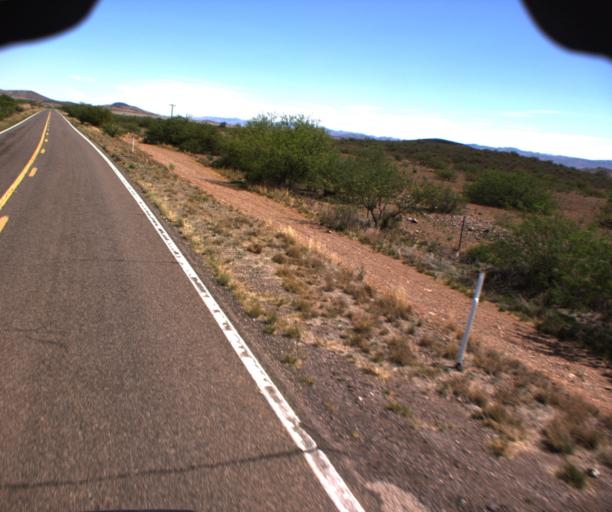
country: US
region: Arizona
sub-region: Cochise County
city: Douglas
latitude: 31.5074
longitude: -109.3148
